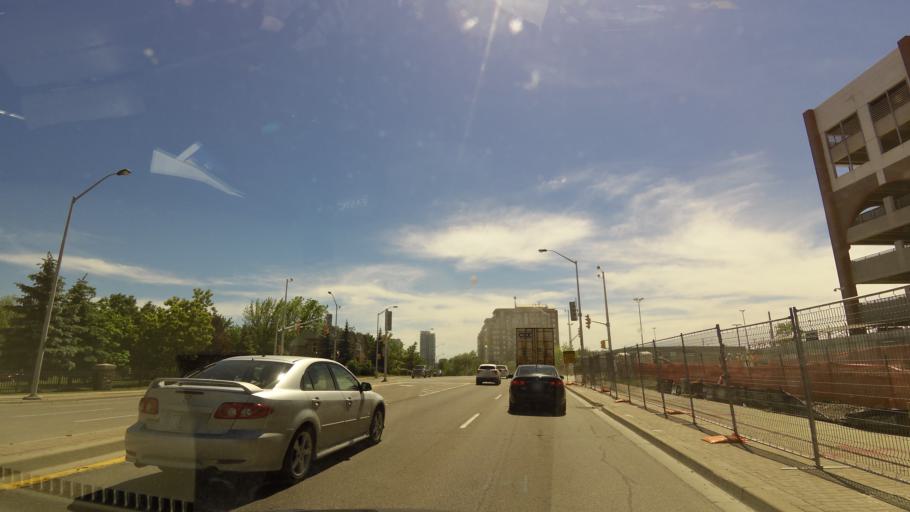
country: CA
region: Ontario
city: Oakville
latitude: 43.4544
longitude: -79.6814
